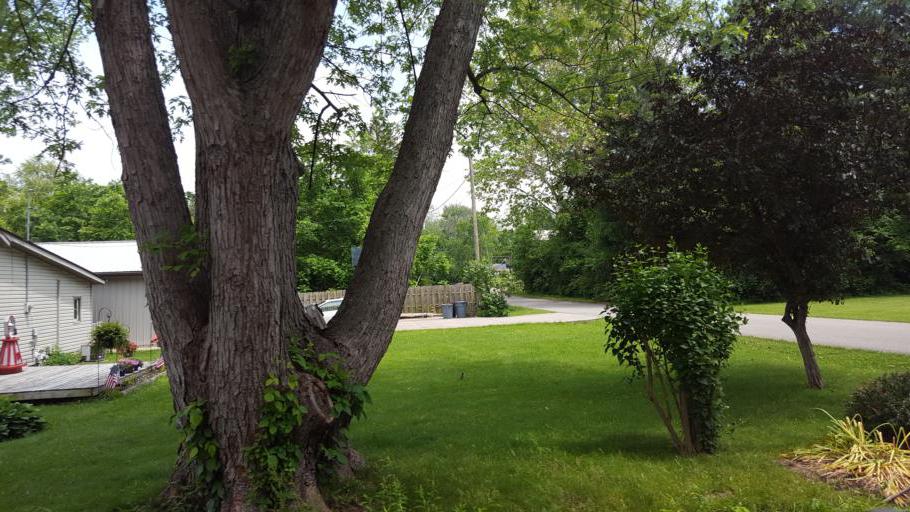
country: US
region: Ohio
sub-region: Fairfield County
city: Fairfield Beach
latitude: 39.9192
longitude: -82.4751
